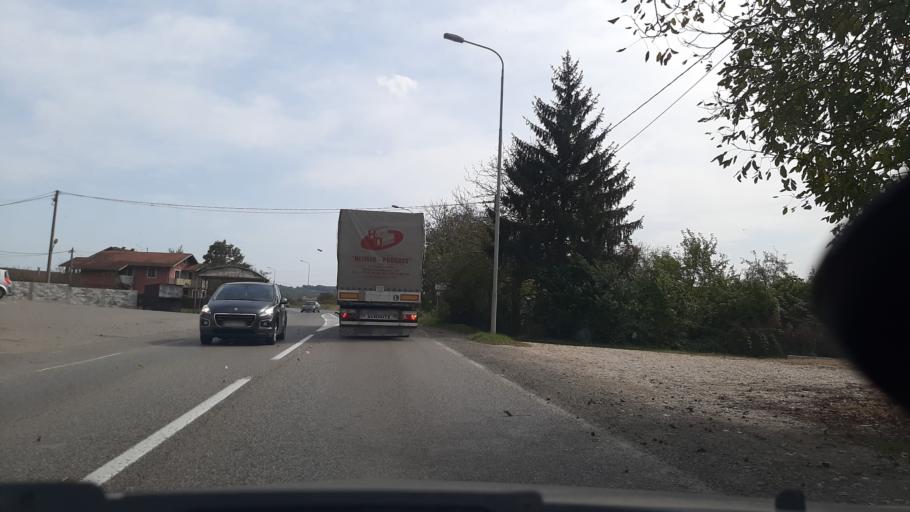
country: BA
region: Republika Srpska
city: Laktasi
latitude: 44.8784
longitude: 17.2905
